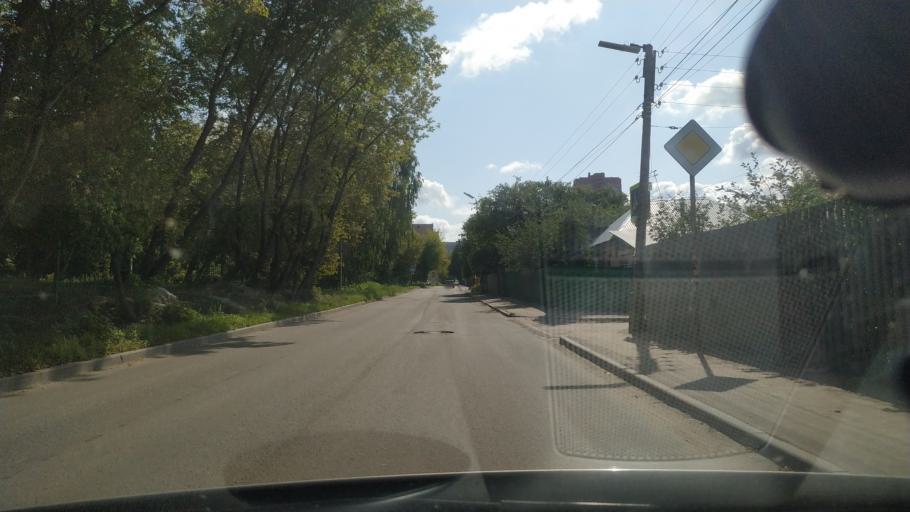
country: RU
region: Rjazan
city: Ryazan'
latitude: 54.6168
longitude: 39.7077
